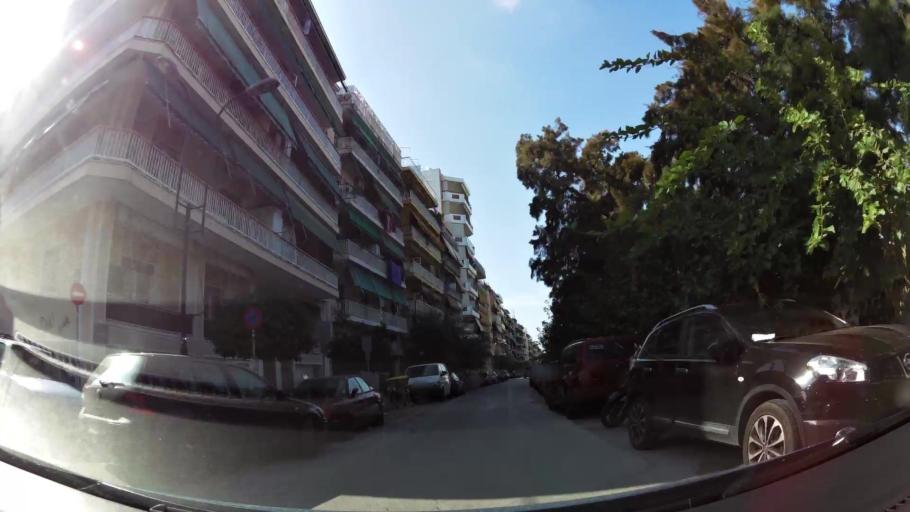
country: GR
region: Attica
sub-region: Nomarchia Athinas
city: Kaisariani
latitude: 37.9842
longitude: 23.7700
